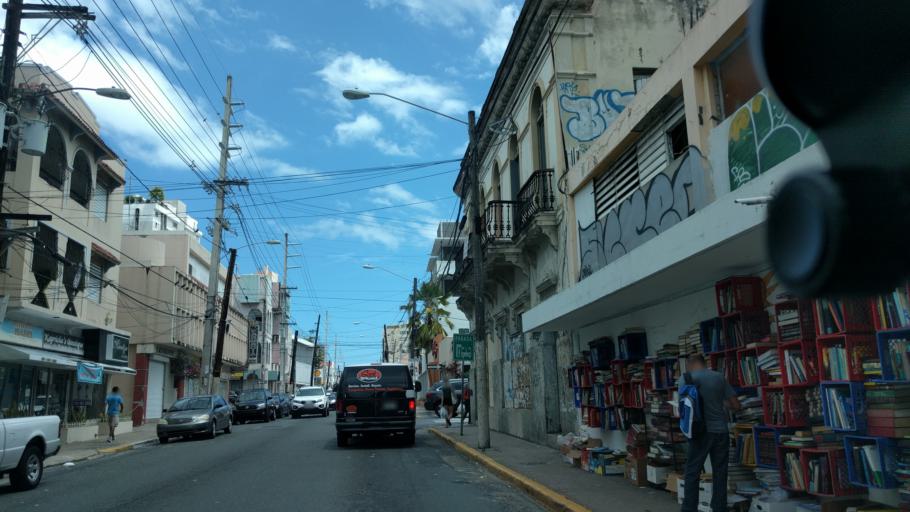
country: PR
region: San Juan
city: San Juan
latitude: 18.4519
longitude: -66.0630
